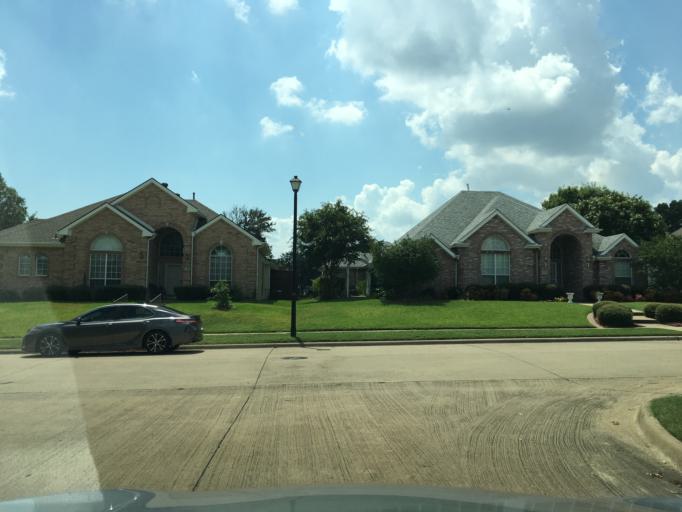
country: US
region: Texas
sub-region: Dallas County
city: Garland
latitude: 32.9410
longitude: -96.6464
